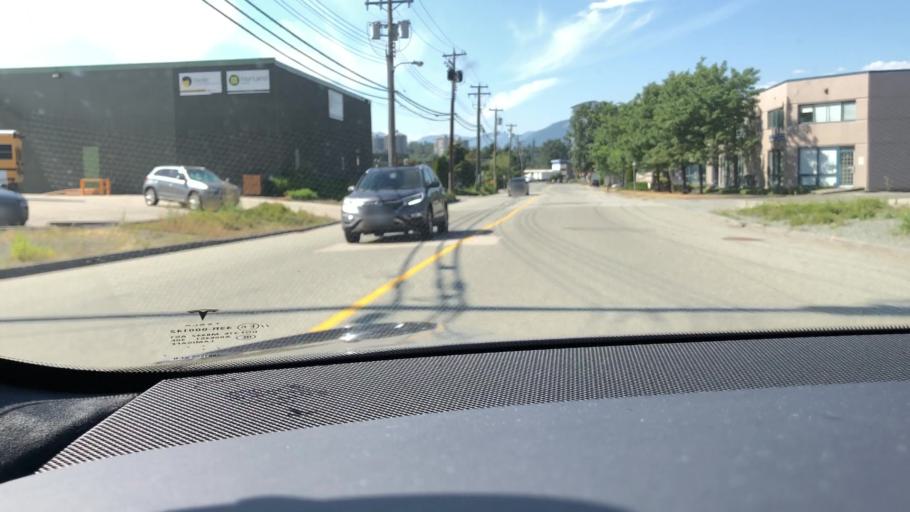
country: CA
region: British Columbia
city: Burnaby
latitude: 49.2555
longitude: -122.9758
